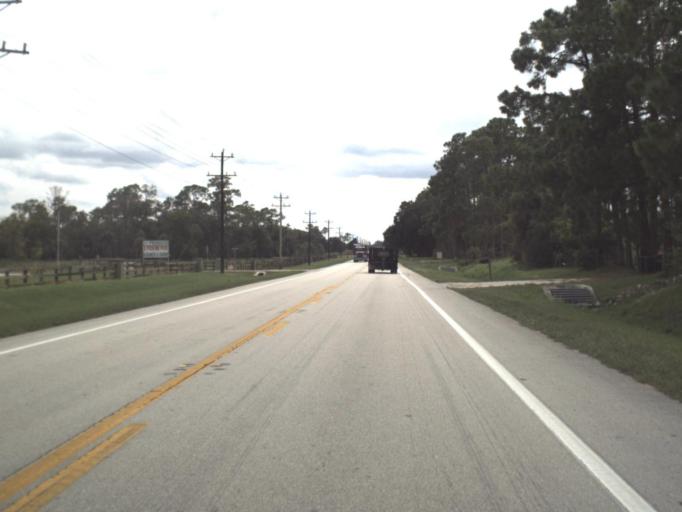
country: US
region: Florida
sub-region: Lee County
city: Fort Myers Shores
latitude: 26.7361
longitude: -81.7611
